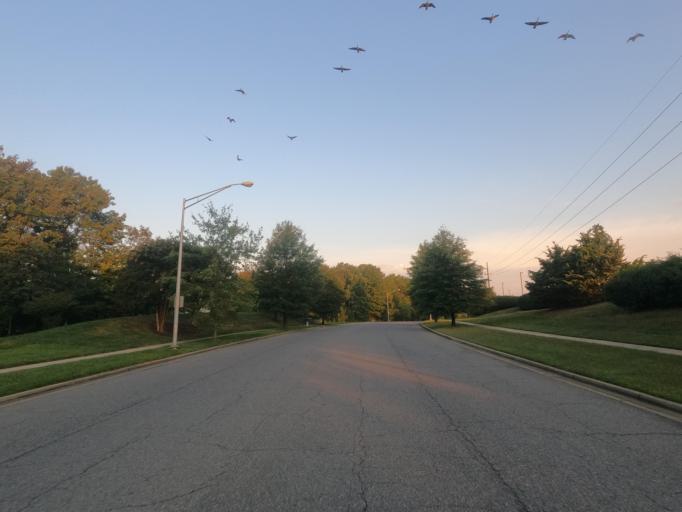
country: US
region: Maryland
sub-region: Prince George's County
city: Accokeek
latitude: 38.6590
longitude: -77.0168
